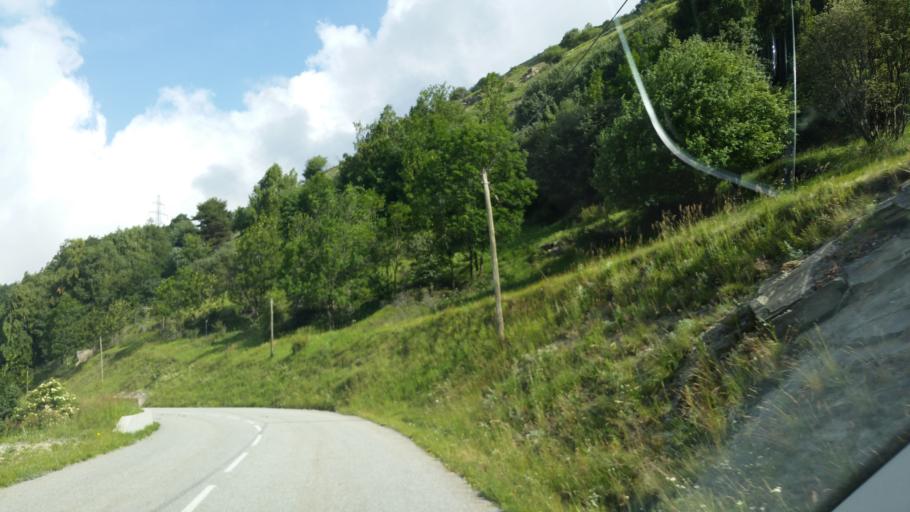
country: FR
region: Rhone-Alpes
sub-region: Departement de la Savoie
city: Modane
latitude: 45.2056
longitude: 6.6108
